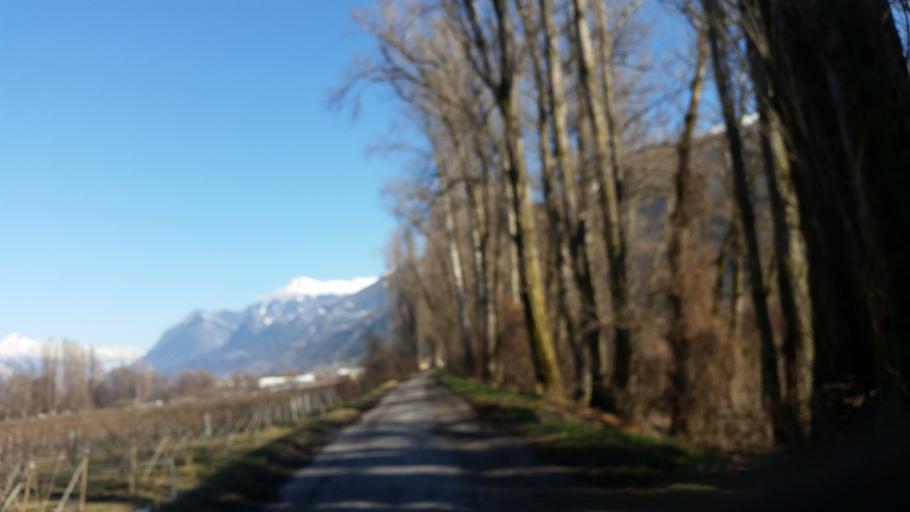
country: CH
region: Valais
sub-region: Sion District
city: Saint-Leonard
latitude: 46.2452
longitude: 7.3998
